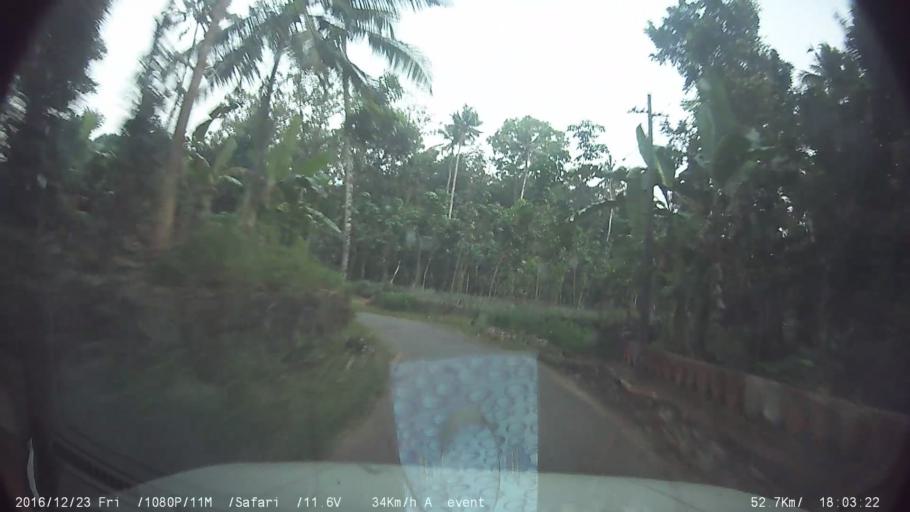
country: IN
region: Kerala
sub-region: Kottayam
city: Palackattumala
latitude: 9.7785
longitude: 76.5870
